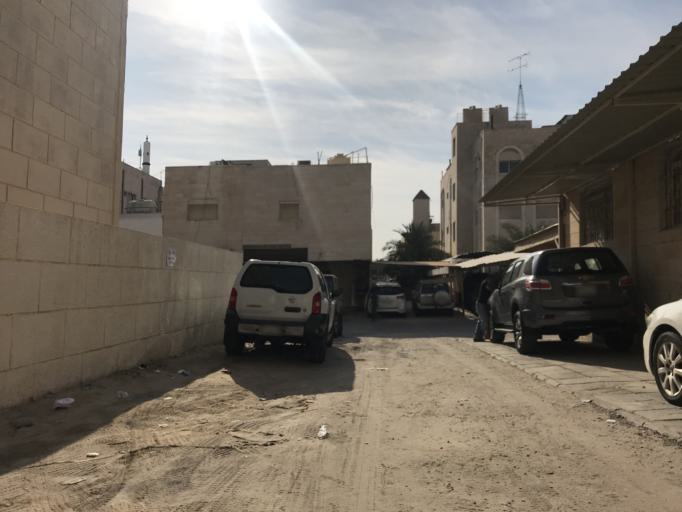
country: KW
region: Muhafazat Hawalli
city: Ar Rumaythiyah
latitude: 29.3046
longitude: 48.0742
